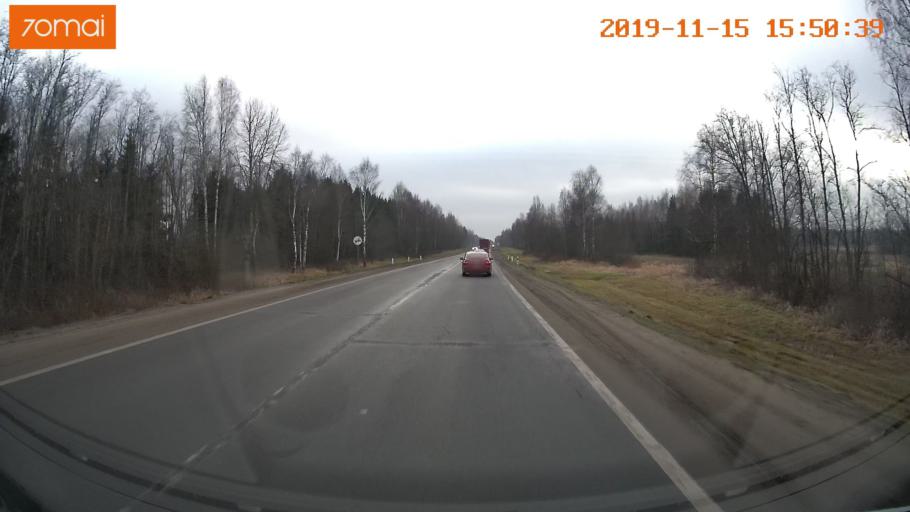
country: RU
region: Jaroslavl
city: Yaroslavl
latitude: 57.9033
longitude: 40.0130
